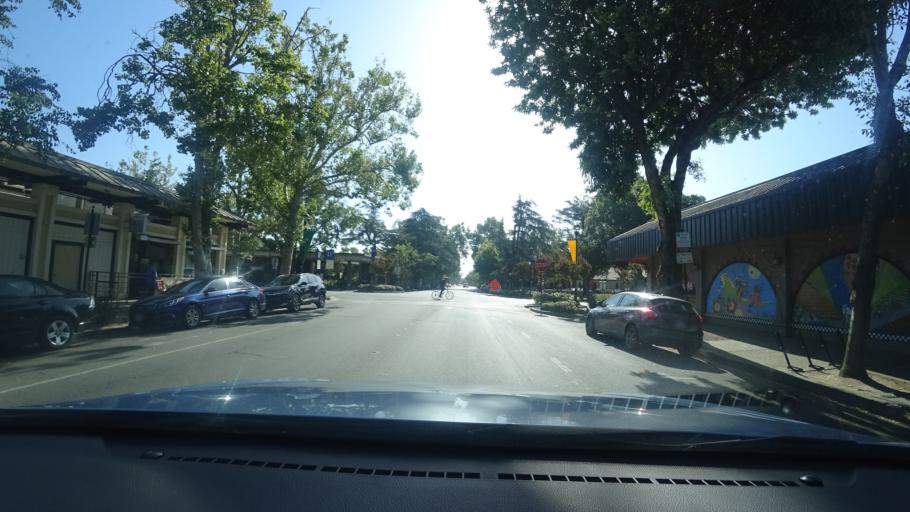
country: US
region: California
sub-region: Yolo County
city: Davis
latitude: 38.5446
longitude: -121.7408
